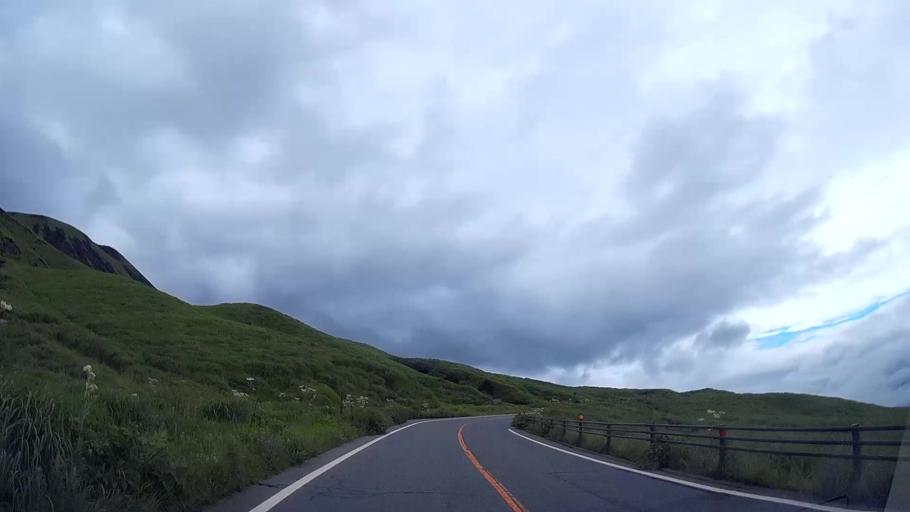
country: JP
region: Kumamoto
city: Aso
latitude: 32.9068
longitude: 131.0599
